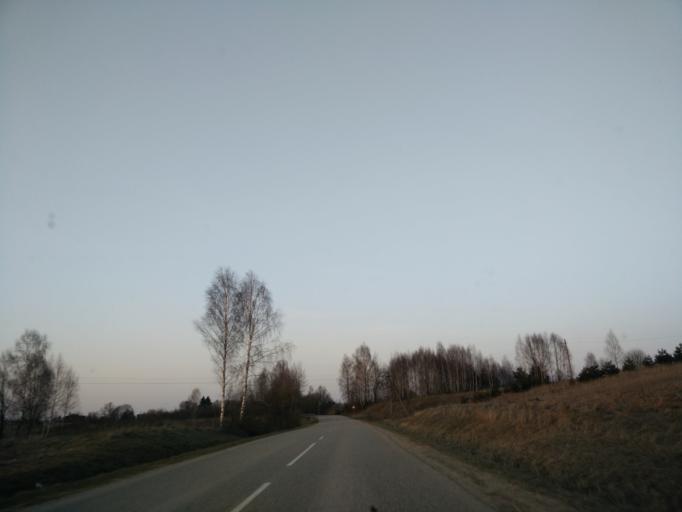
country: LT
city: Trakai
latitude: 54.6841
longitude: 24.9558
